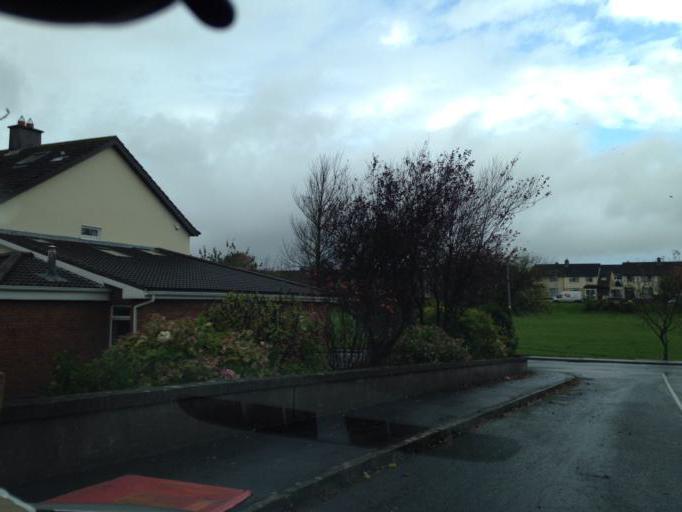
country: IE
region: Connaught
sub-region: County Galway
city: Gaillimh
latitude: 53.2732
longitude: -9.0235
